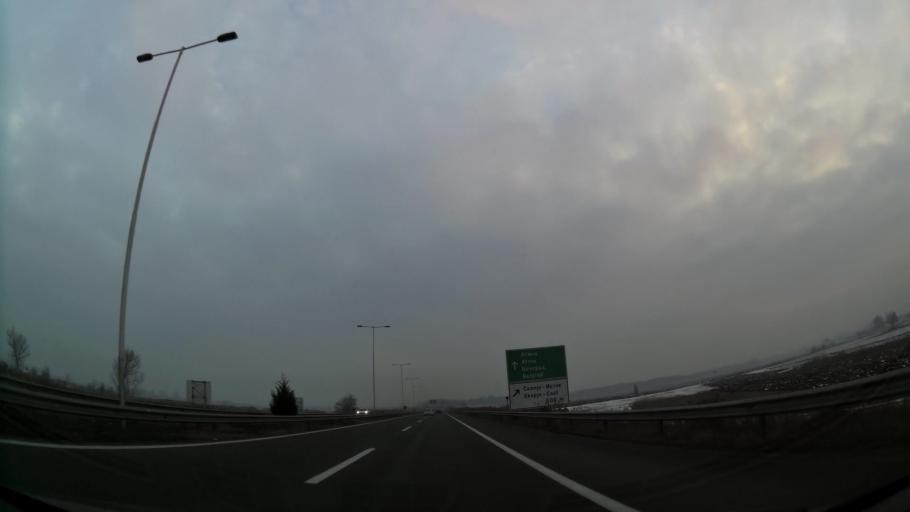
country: MK
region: Aracinovo
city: Arachinovo
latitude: 42.0032
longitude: 21.5342
